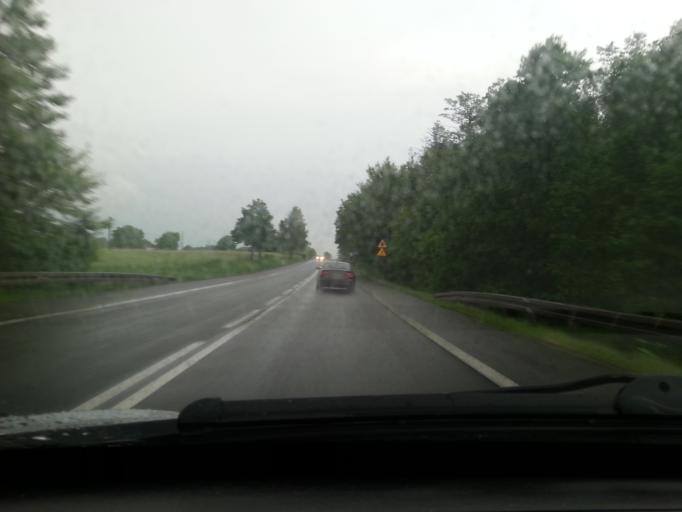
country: PL
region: Lodz Voivodeship
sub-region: Powiat zgierski
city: Strykow
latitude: 51.8695
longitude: 19.5718
